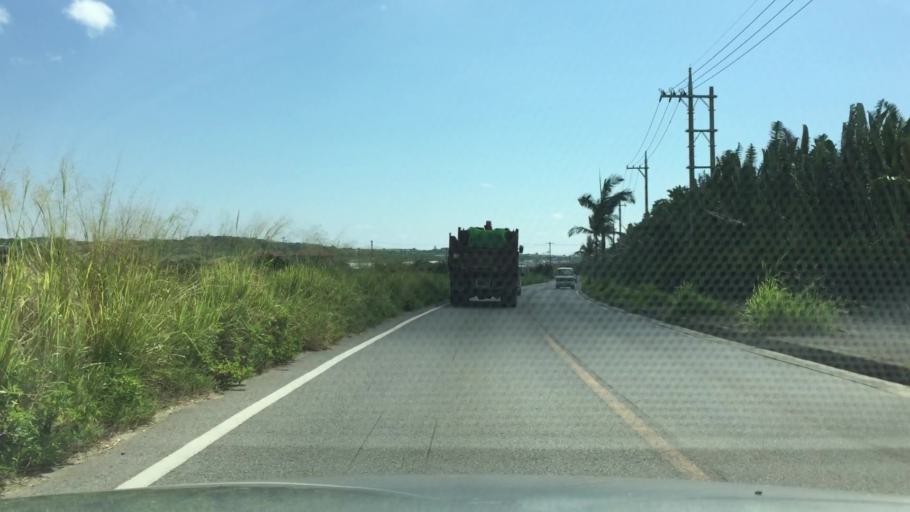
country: JP
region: Okinawa
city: Ishigaki
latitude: 24.3561
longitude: 124.1960
